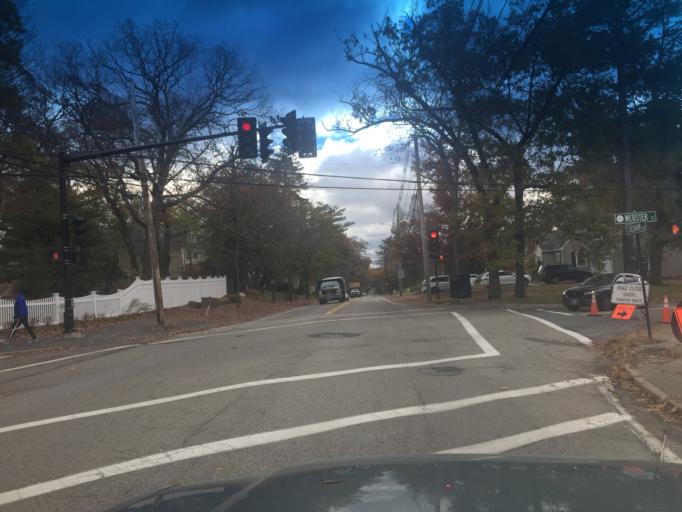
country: US
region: Massachusetts
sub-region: Norfolk County
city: Needham
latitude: 42.2765
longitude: -71.2308
